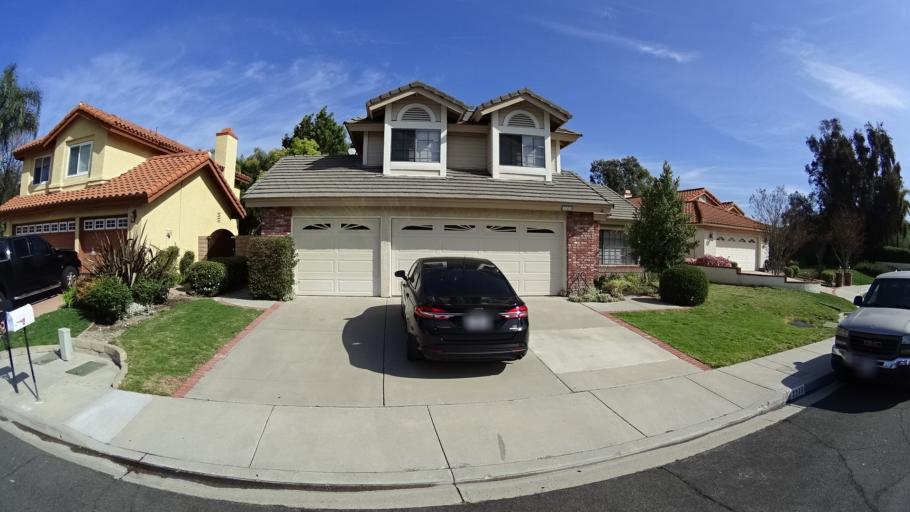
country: US
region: California
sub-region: Ventura County
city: Thousand Oaks
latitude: 34.2150
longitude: -118.8373
